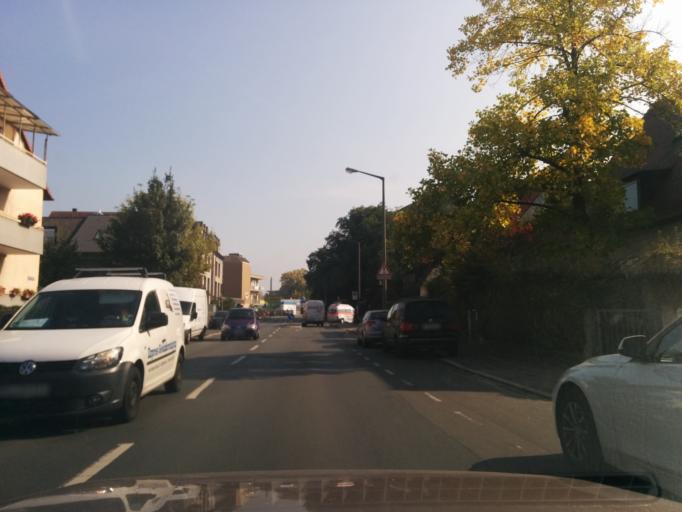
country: DE
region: Bavaria
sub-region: Regierungsbezirk Mittelfranken
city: Nuernberg
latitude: 49.4745
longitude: 11.1000
